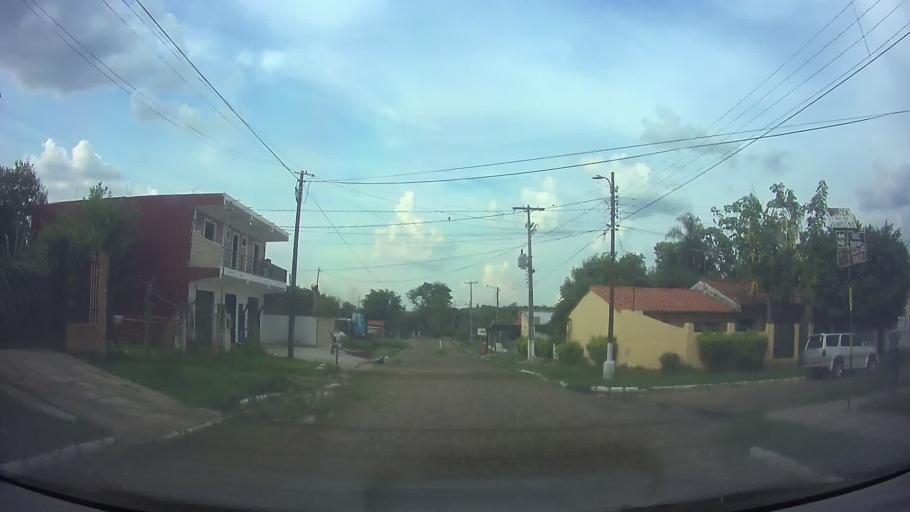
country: PY
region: Central
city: San Lorenzo
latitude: -25.2660
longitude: -57.4766
